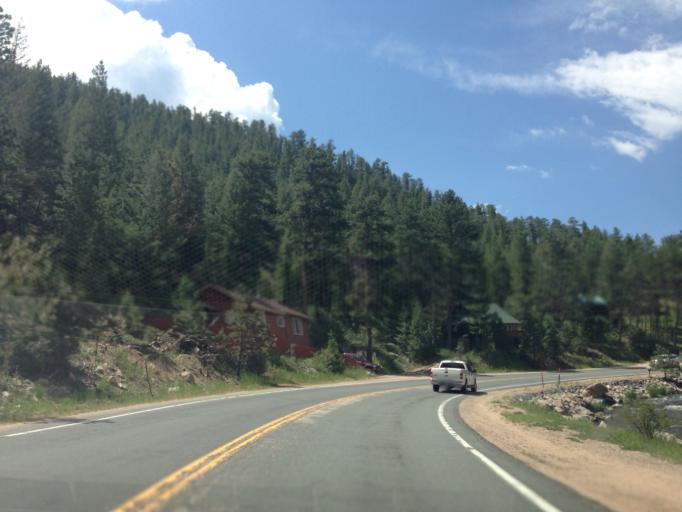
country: US
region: Colorado
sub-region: Larimer County
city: Estes Park
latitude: 40.3859
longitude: -105.4674
